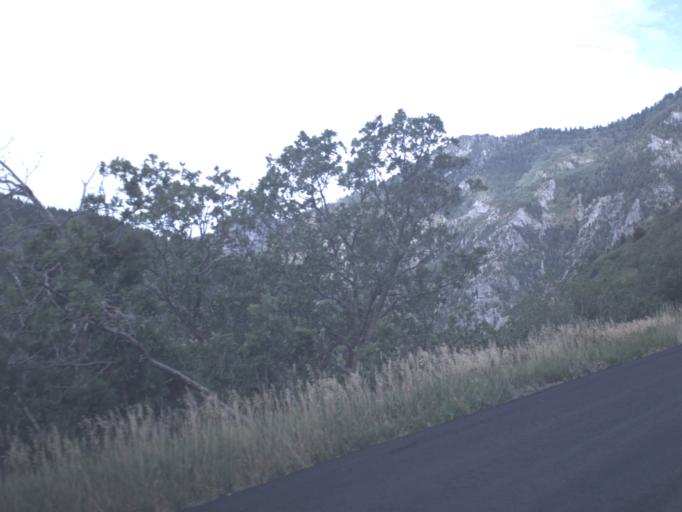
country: US
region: Utah
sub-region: Utah County
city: Cedar Hills
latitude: 40.4498
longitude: -111.6441
